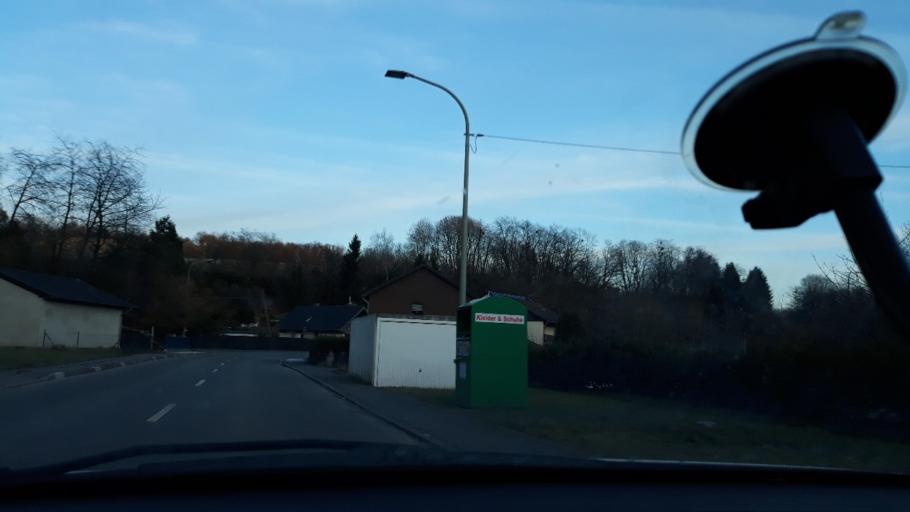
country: DE
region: Saarland
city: Sankt Ingbert
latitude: 49.2245
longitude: 7.1441
